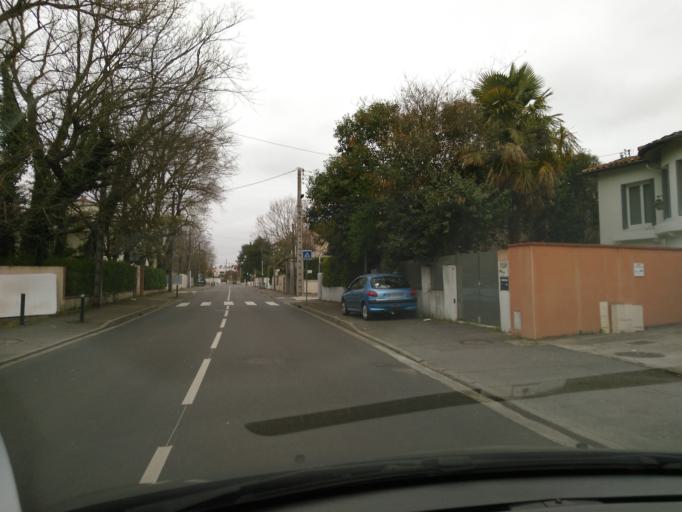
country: FR
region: Midi-Pyrenees
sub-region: Departement de la Haute-Garonne
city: Balma
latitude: 43.5830
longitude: 1.4790
